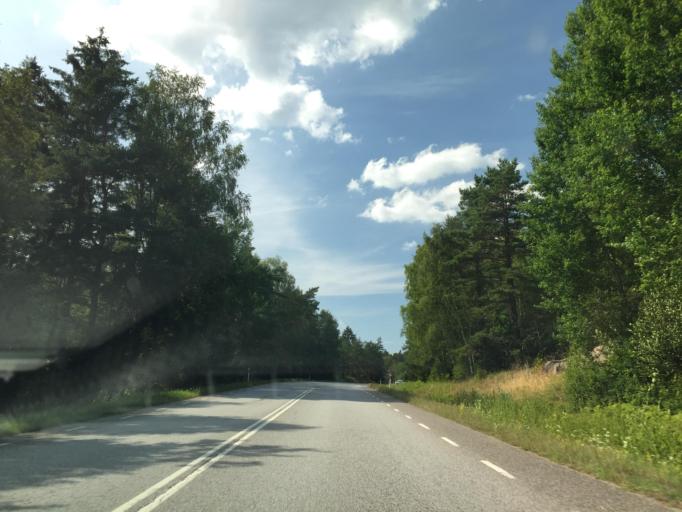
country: SE
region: Vaestra Goetaland
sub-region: Tanums Kommun
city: Grebbestad
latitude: 58.8224
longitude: 11.2551
